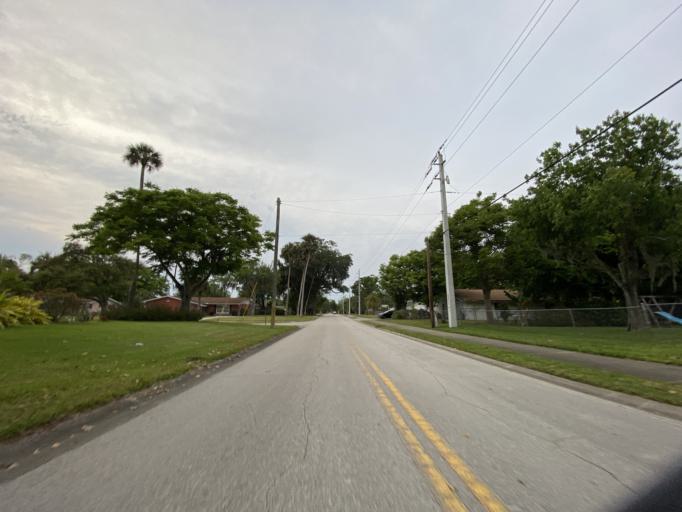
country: US
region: Florida
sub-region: Volusia County
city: South Daytona
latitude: 29.1594
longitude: -81.0132
